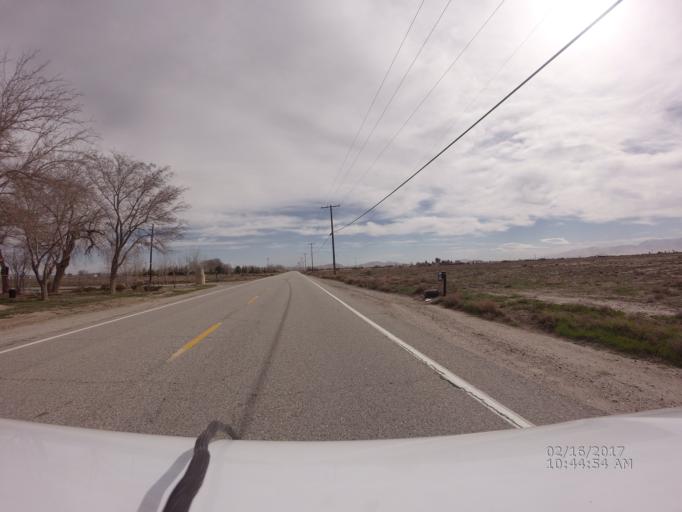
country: US
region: California
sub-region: Los Angeles County
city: Lake Los Angeles
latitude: 34.7195
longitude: -117.9568
